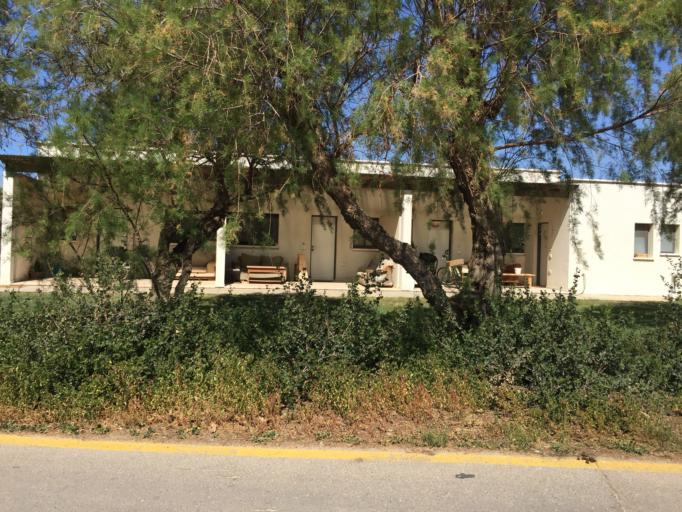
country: IL
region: Haifa
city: Qesarya
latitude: 32.4900
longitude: 34.8906
